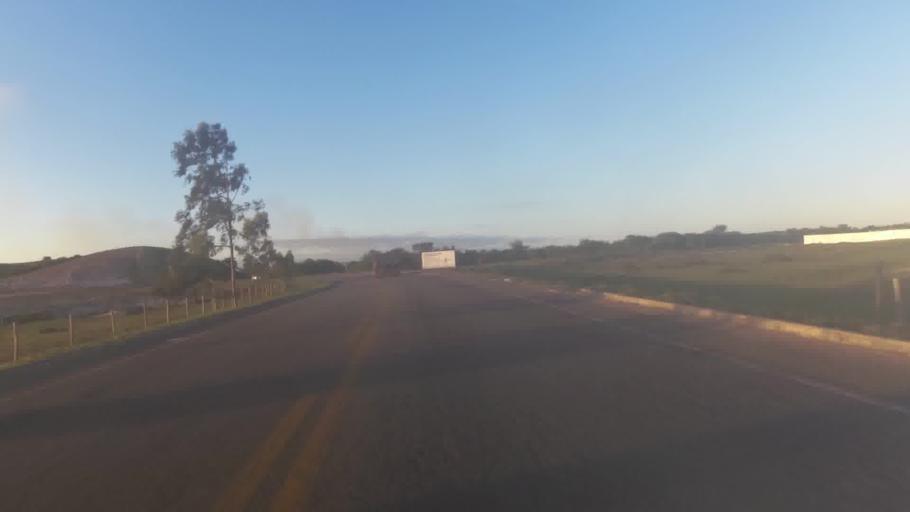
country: BR
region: Espirito Santo
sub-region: Marataizes
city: Marataizes
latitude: -21.1936
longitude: -40.9424
